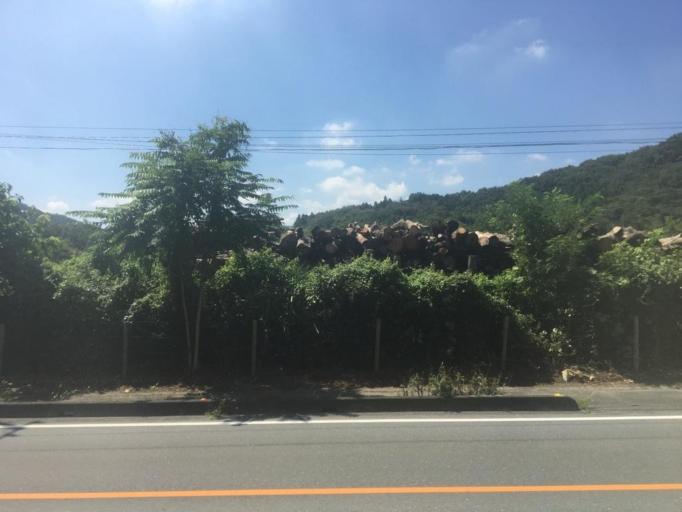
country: JP
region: Saitama
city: Yorii
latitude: 36.1348
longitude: 139.1545
